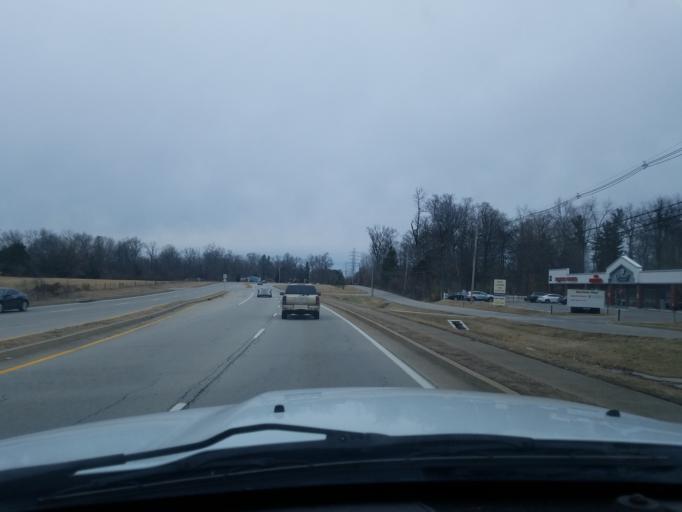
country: US
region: Kentucky
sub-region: Jefferson County
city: Douglass Hills
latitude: 38.2314
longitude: -85.5427
